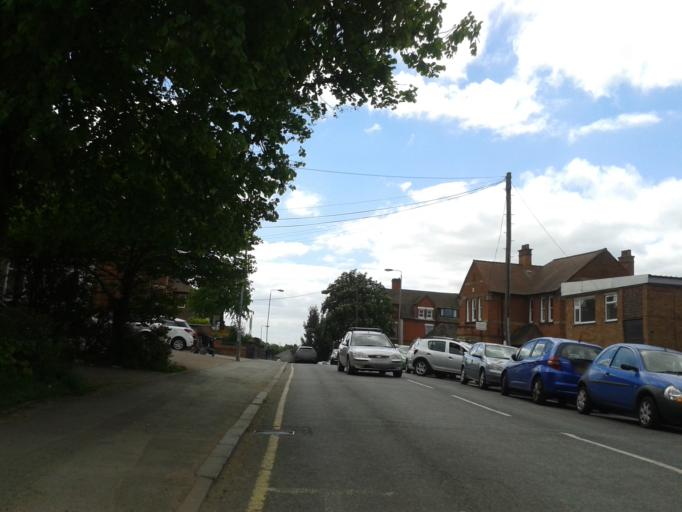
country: GB
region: England
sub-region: Leicestershire
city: Hinckley
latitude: 52.5385
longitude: -1.3727
